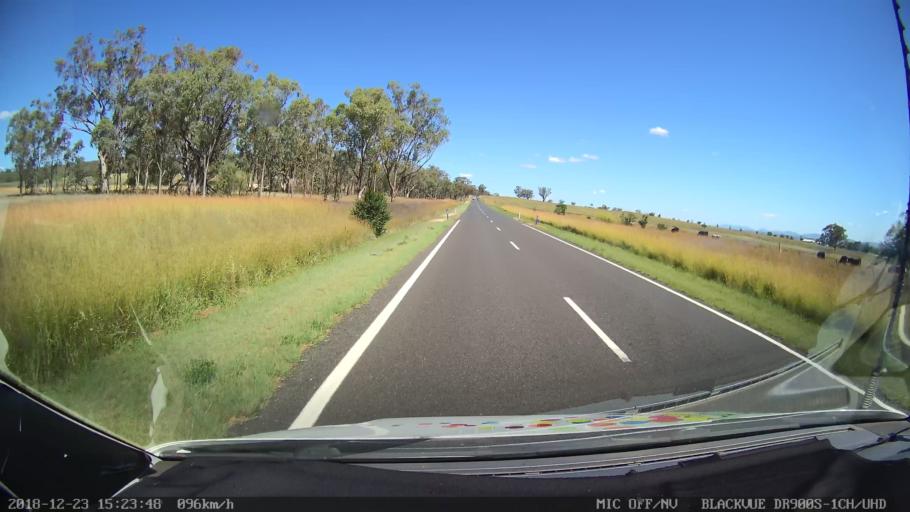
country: AU
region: New South Wales
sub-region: Tamworth Municipality
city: Manilla
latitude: -30.8845
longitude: 150.8176
